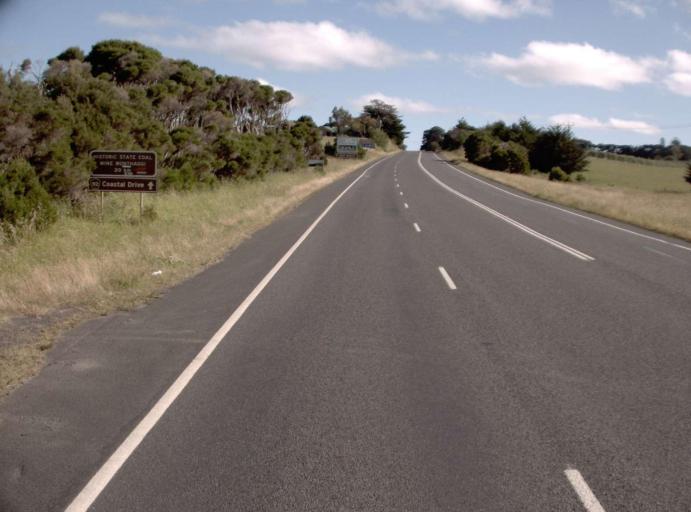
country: AU
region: Victoria
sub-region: Bass Coast
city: North Wonthaggi
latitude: -38.5190
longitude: 145.4481
